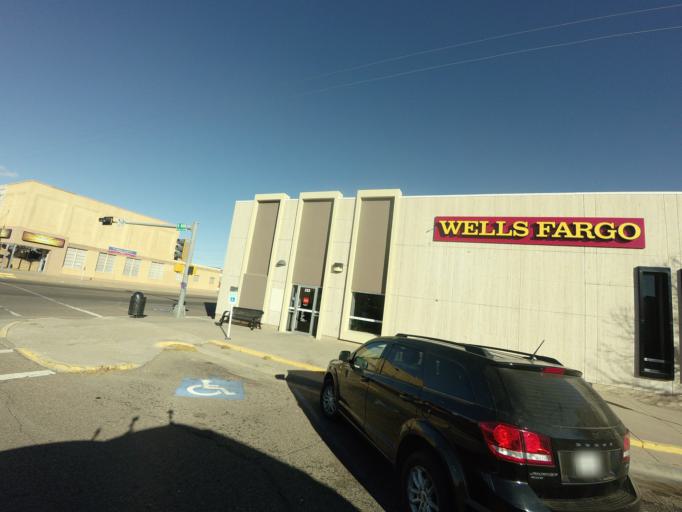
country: US
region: New Mexico
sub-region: Curry County
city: Clovis
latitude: 34.4005
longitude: -103.2053
